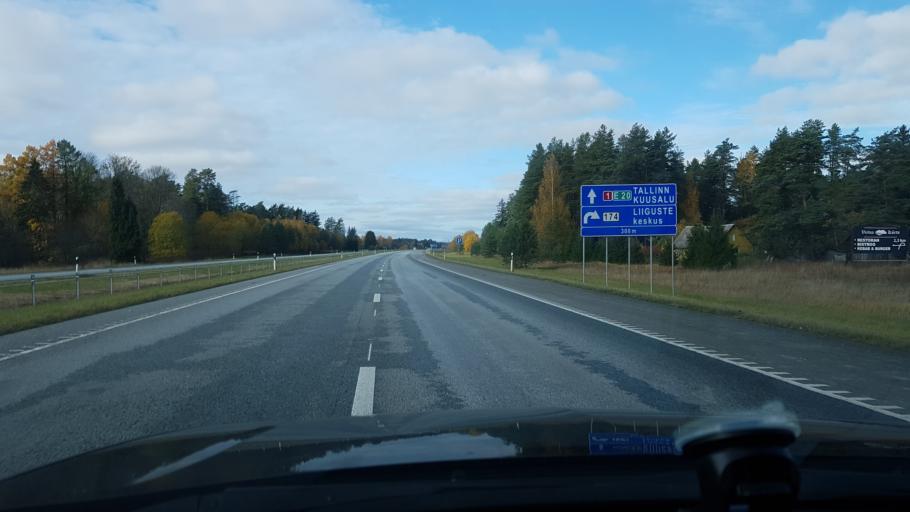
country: EE
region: Laeaene-Virumaa
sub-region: Kadrina vald
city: Kadrina
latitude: 59.4471
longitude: 26.0813
